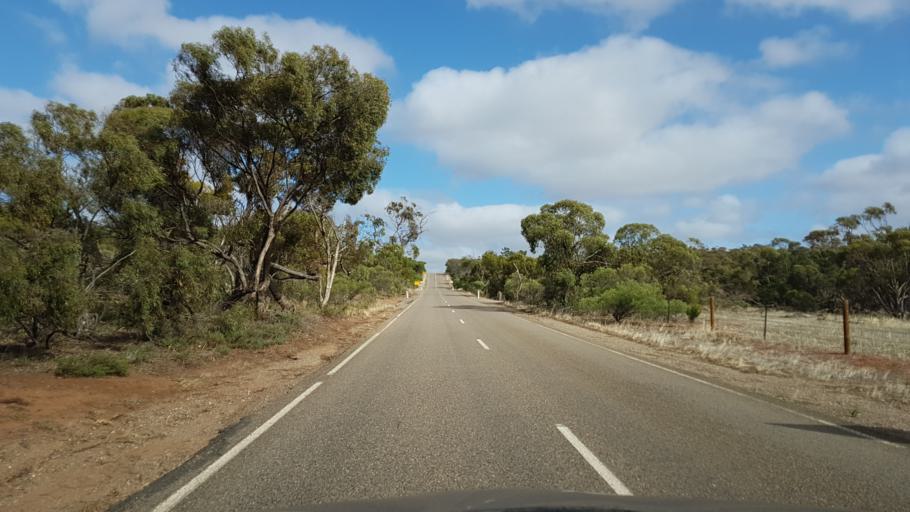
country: AU
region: South Australia
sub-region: Murray Bridge
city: Murray Bridge
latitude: -35.1149
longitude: 139.2300
